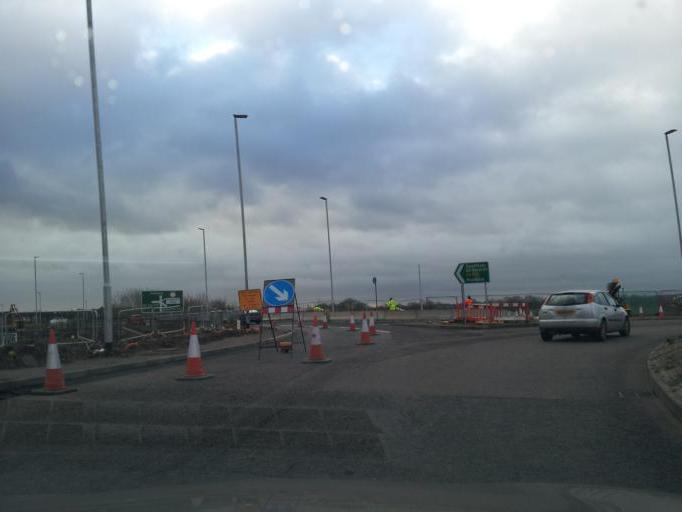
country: GB
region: England
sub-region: Norfolk
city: Surlingham
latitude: 52.6270
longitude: 1.3789
